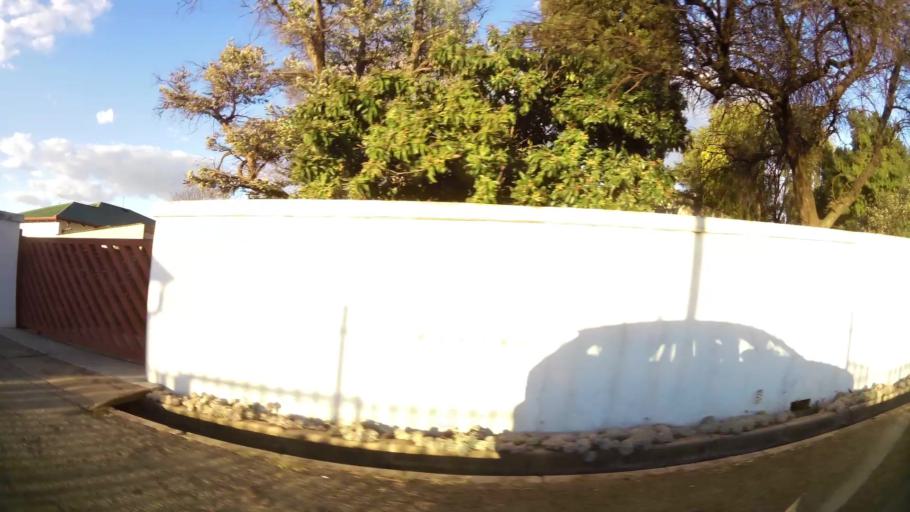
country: ZA
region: North-West
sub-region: Dr Kenneth Kaunda District Municipality
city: Potchefstroom
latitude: -26.7182
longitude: 27.0916
